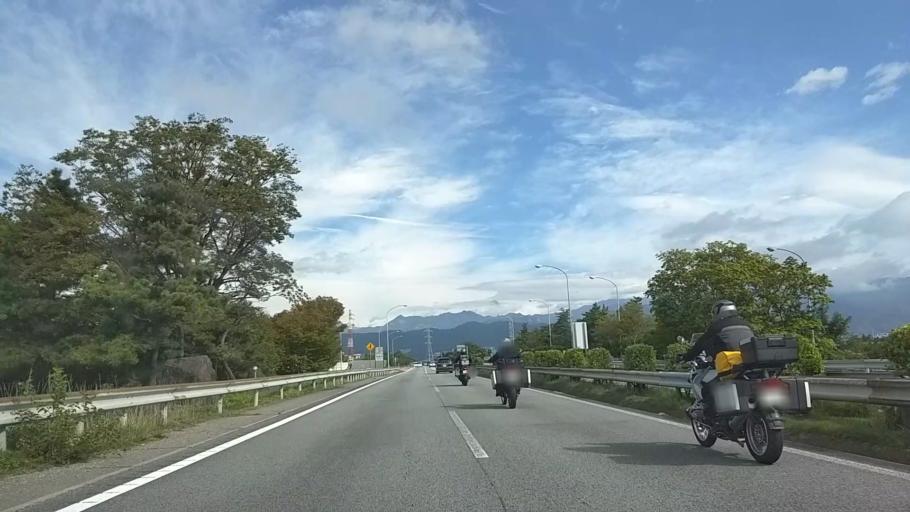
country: JP
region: Yamanashi
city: Kofu-shi
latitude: 35.6437
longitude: 138.5373
